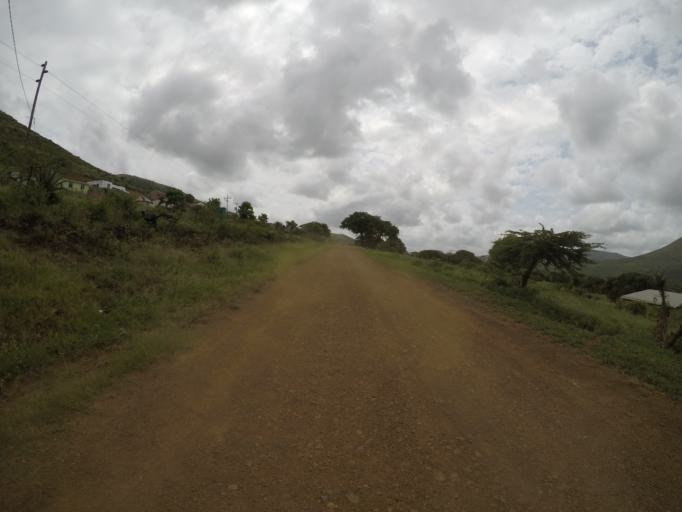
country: ZA
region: KwaZulu-Natal
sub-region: uThungulu District Municipality
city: Empangeni
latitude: -28.5940
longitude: 31.8808
